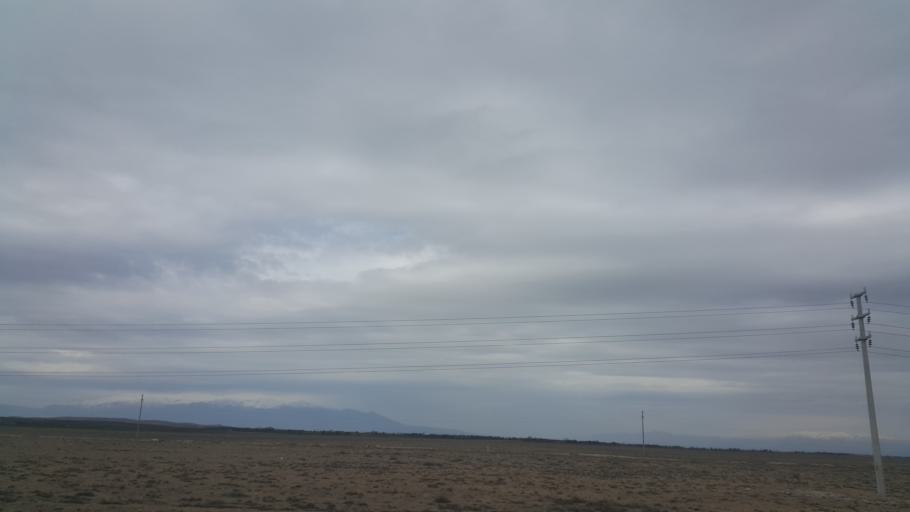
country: TR
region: Nigde
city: Altunhisar
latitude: 37.7822
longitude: 34.2352
